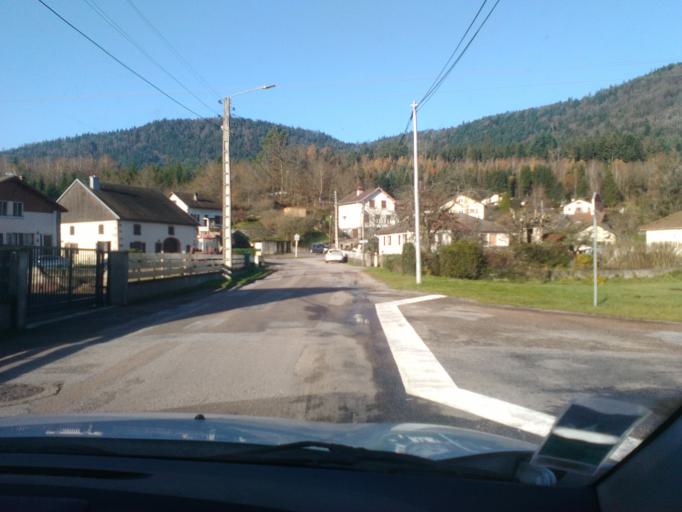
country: FR
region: Lorraine
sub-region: Departement des Vosges
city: Saint-Ame
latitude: 48.0231
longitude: 6.6587
